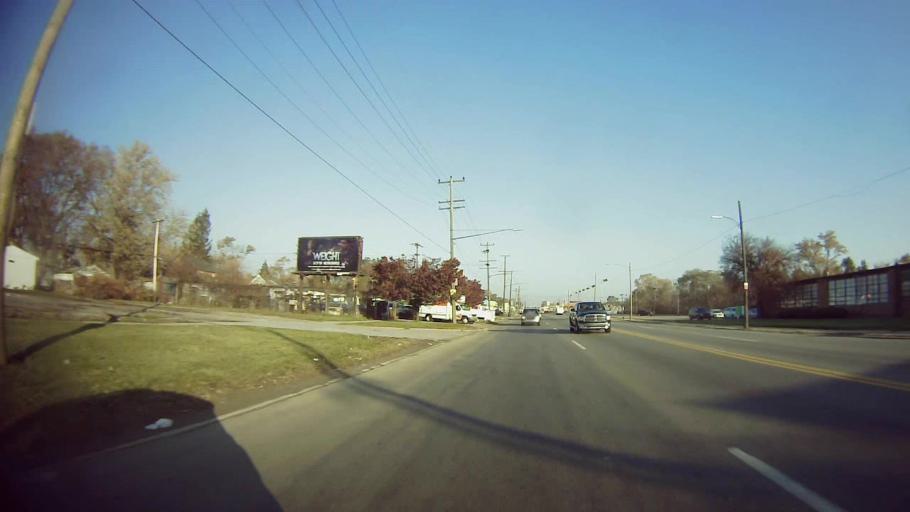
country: US
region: Michigan
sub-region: Wayne County
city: Dearborn
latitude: 42.3842
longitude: -83.1981
